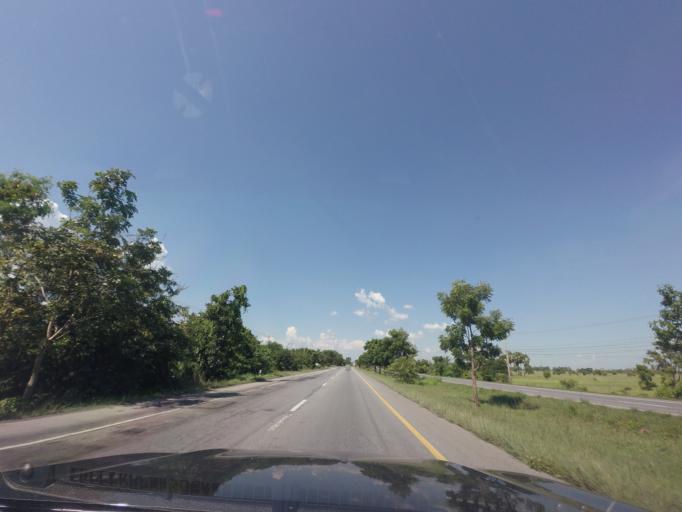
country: TH
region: Nakhon Ratchasima
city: Non Sung
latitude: 15.2181
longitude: 102.3600
